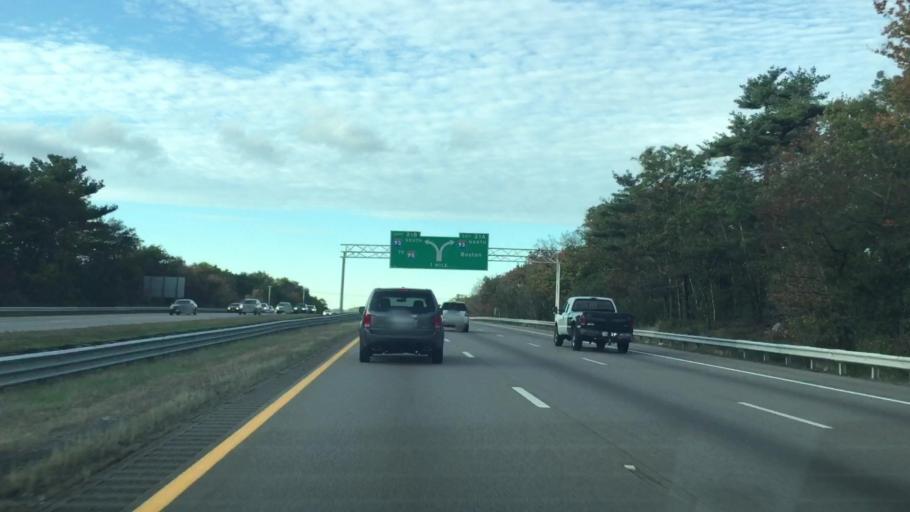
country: US
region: Massachusetts
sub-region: Norfolk County
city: Randolph
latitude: 42.1831
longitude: -71.0760
